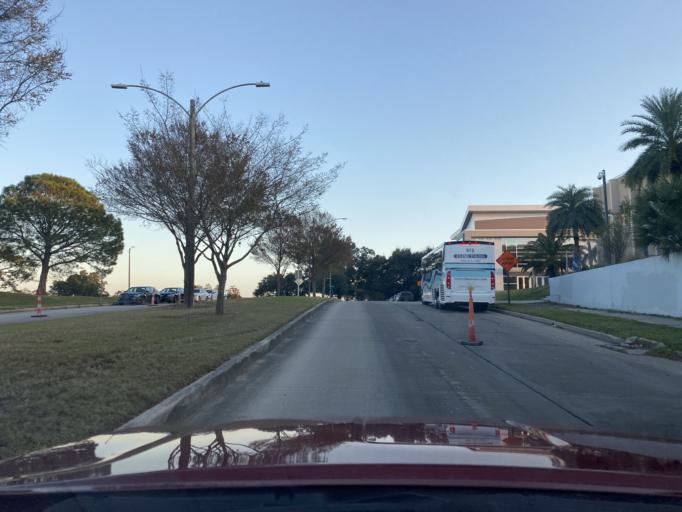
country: US
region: Louisiana
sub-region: Orleans Parish
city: New Orleans
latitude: 30.0278
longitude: -90.0447
